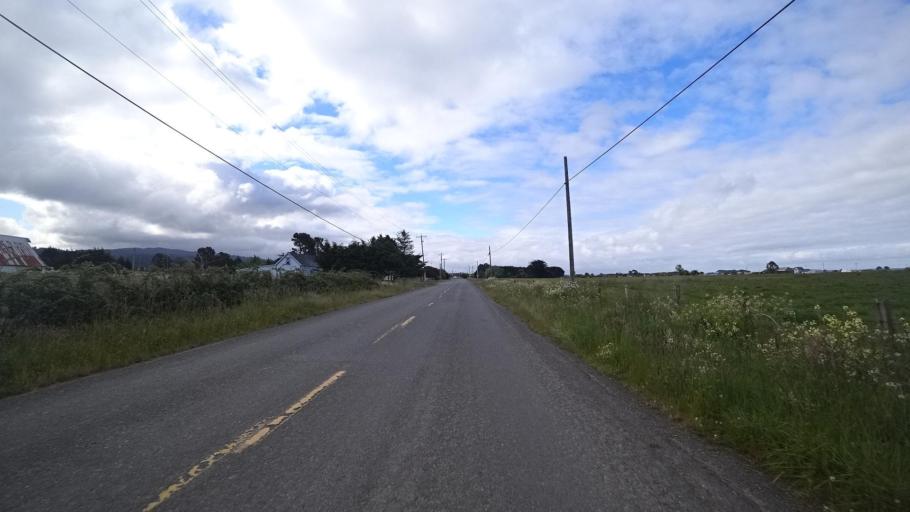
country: US
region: California
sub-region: Humboldt County
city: Arcata
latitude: 40.9059
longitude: -124.0914
